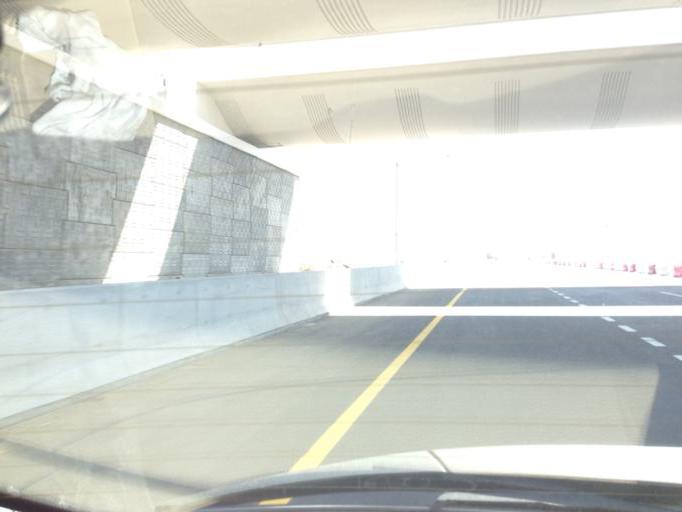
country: OM
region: Al Batinah
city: Rustaq
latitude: 23.5347
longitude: 57.5627
